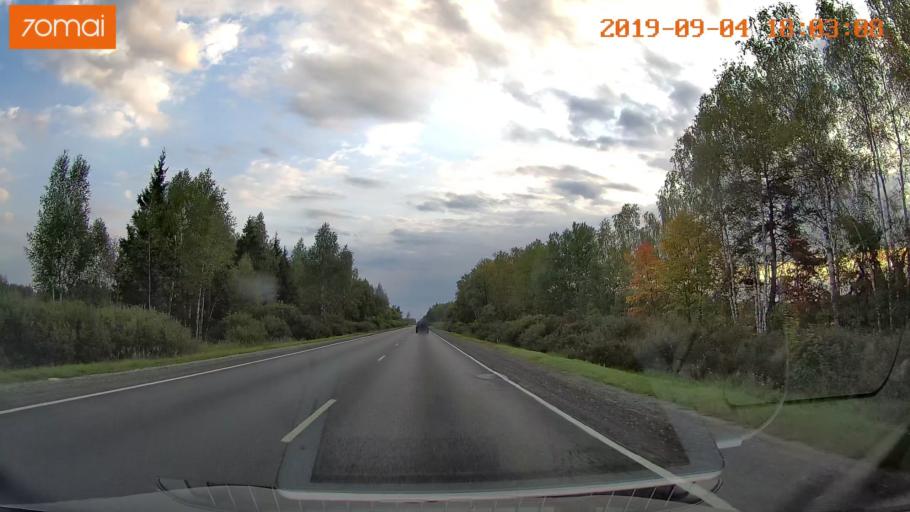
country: RU
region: Moskovskaya
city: Il'inskiy Pogost
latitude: 55.4666
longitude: 38.8559
